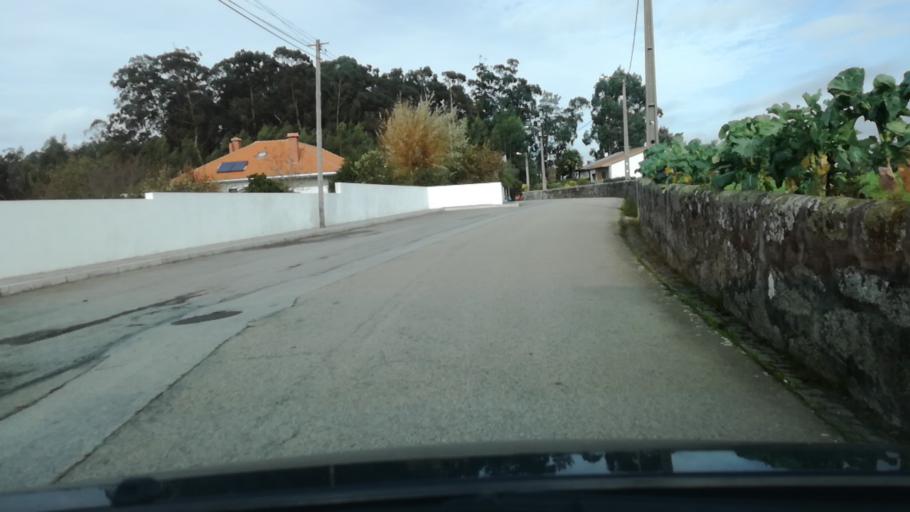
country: PT
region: Porto
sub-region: Maia
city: Gemunde
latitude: 41.2604
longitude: -8.6746
